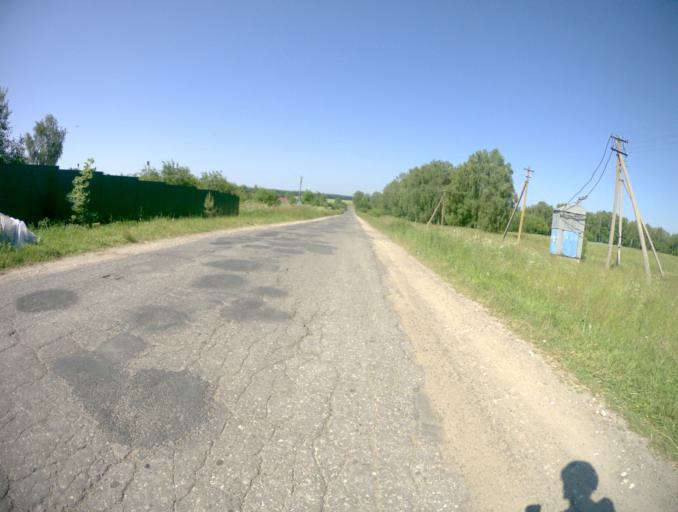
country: RU
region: Vladimir
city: Novovyazniki
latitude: 56.2299
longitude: 42.2434
